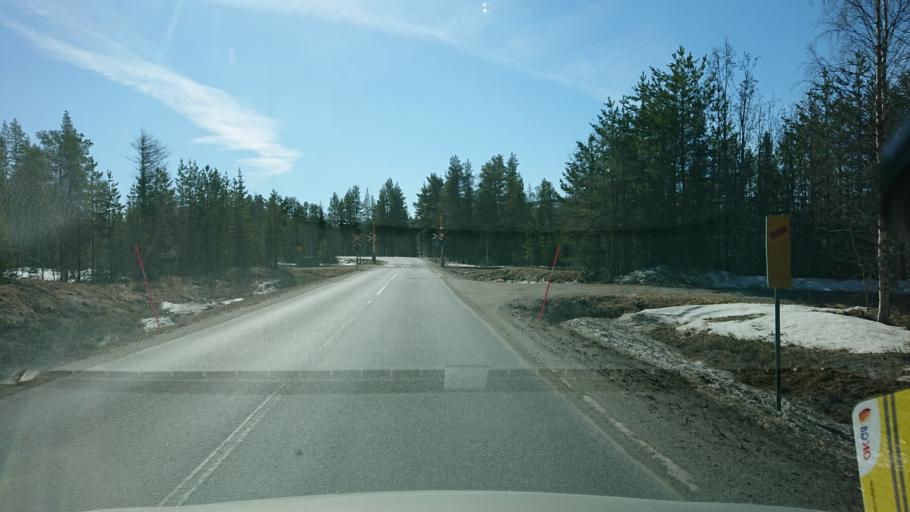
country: SE
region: Vaesterbotten
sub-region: Dorotea Kommun
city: Dorotea
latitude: 64.0109
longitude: 16.2945
